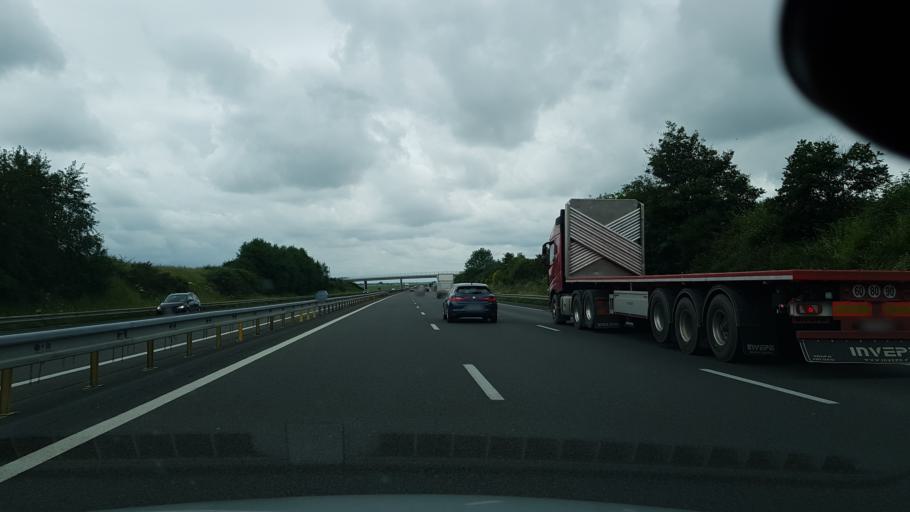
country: FR
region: Centre
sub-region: Departement du Loir-et-Cher
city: Herbault
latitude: 47.5717
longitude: 1.0520
